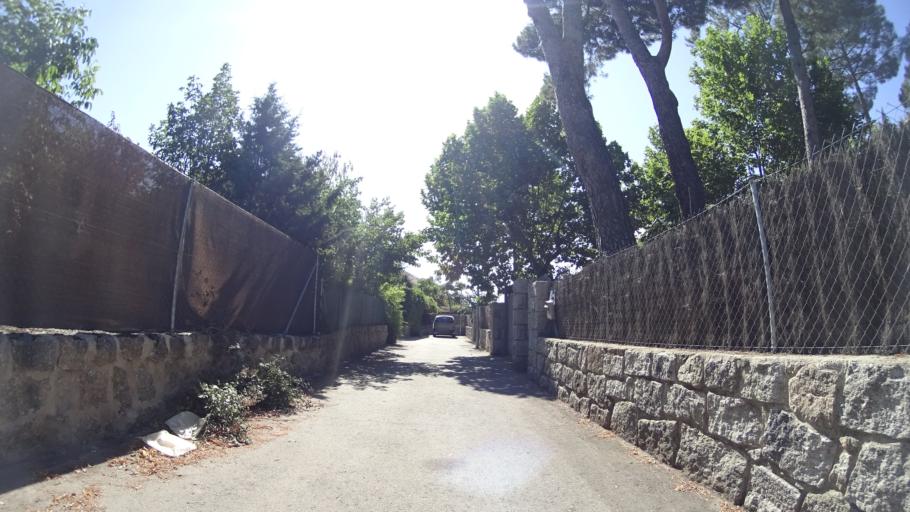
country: ES
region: Madrid
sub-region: Provincia de Madrid
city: Galapagar
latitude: 40.5967
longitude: -3.9830
